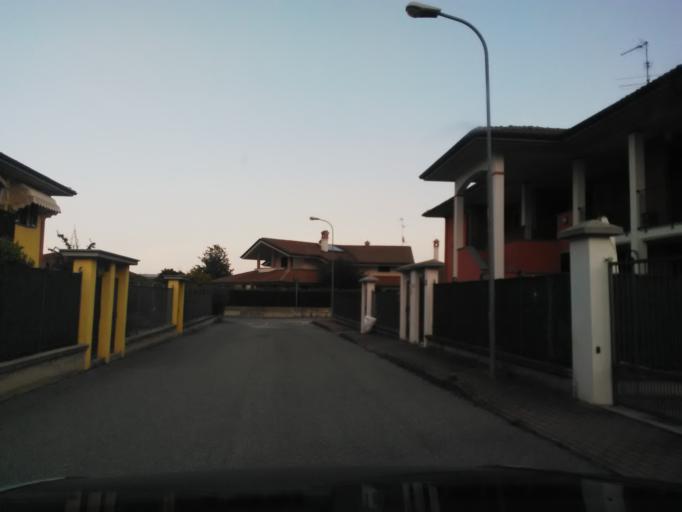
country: IT
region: Piedmont
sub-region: Provincia di Vercelli
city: Cigliano
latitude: 45.3078
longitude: 8.0294
